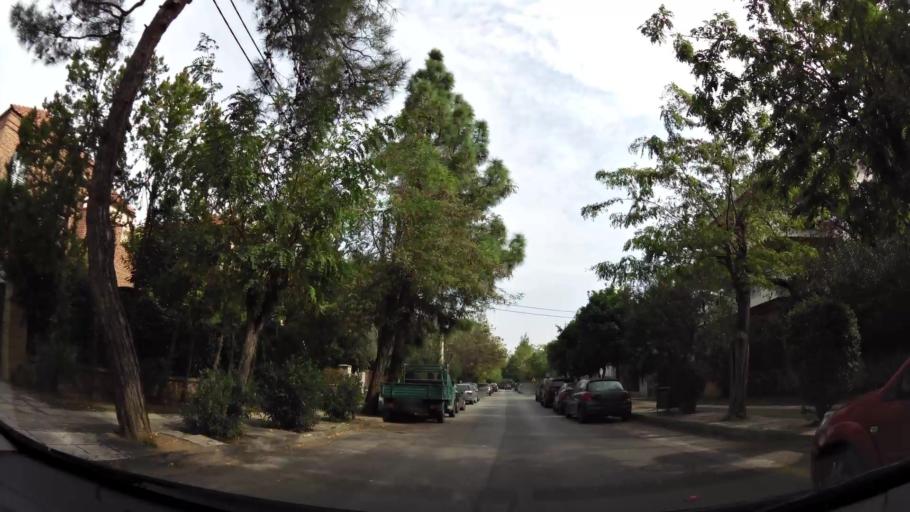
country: GR
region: Attica
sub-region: Nomarchia Athinas
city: Psychiko
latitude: 38.0106
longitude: 23.7739
